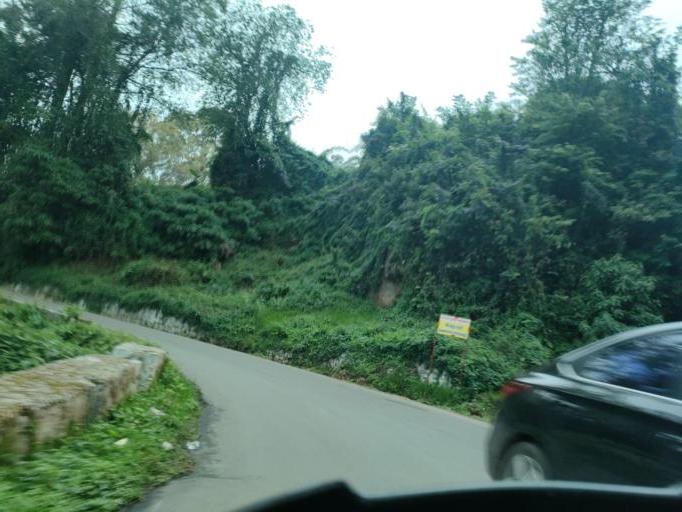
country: IN
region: Tamil Nadu
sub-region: Dindigul
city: Kodaikanal
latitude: 10.2333
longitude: 77.5037
